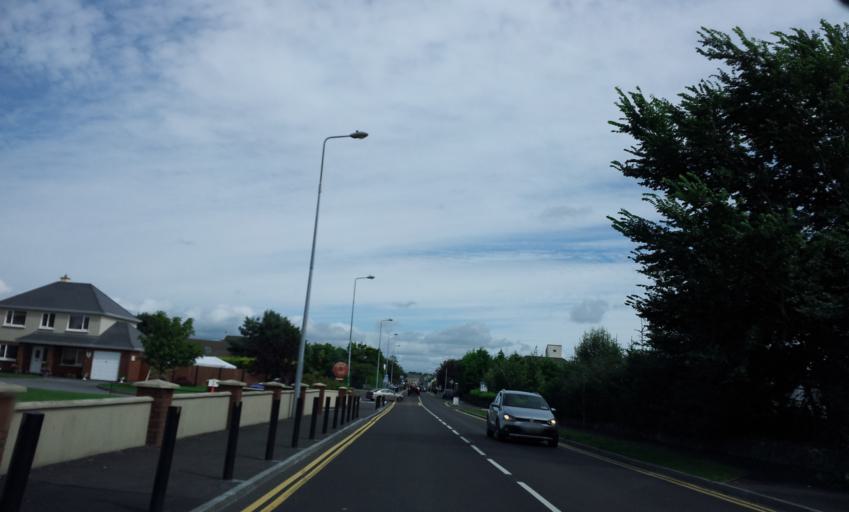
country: IE
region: Munster
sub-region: Ciarrai
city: Killorglin
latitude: 52.1053
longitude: -9.7958
